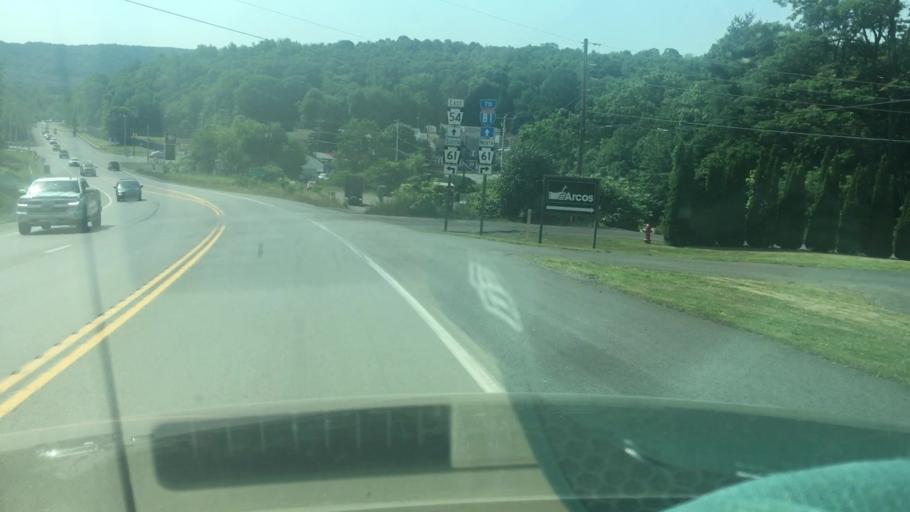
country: US
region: Pennsylvania
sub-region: Northumberland County
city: Mount Carmel
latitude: 40.8007
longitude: -76.4391
